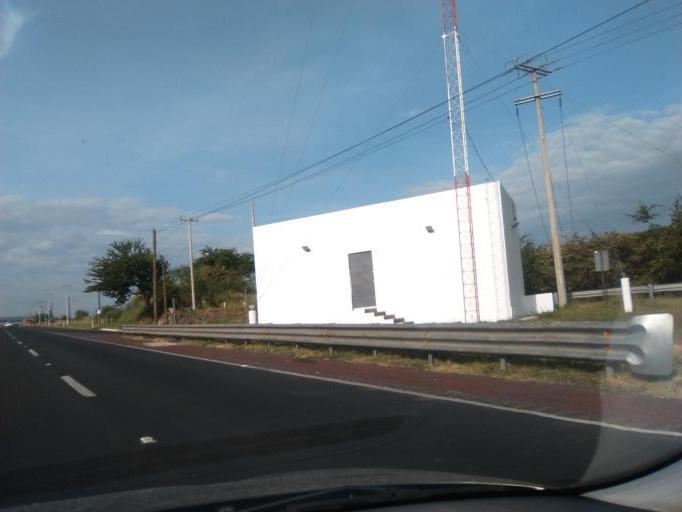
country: MX
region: Morelos
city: Xochitepec
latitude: 18.8028
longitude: -99.2203
